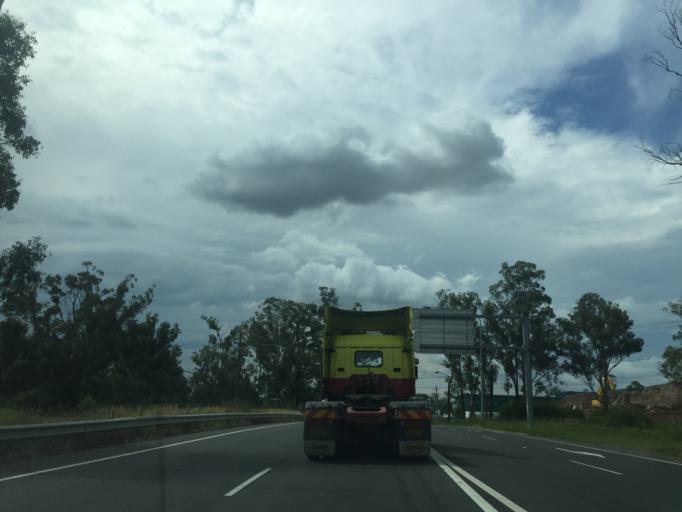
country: AU
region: New South Wales
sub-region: Blacktown
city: Blacktown
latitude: -33.8014
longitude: 150.8962
